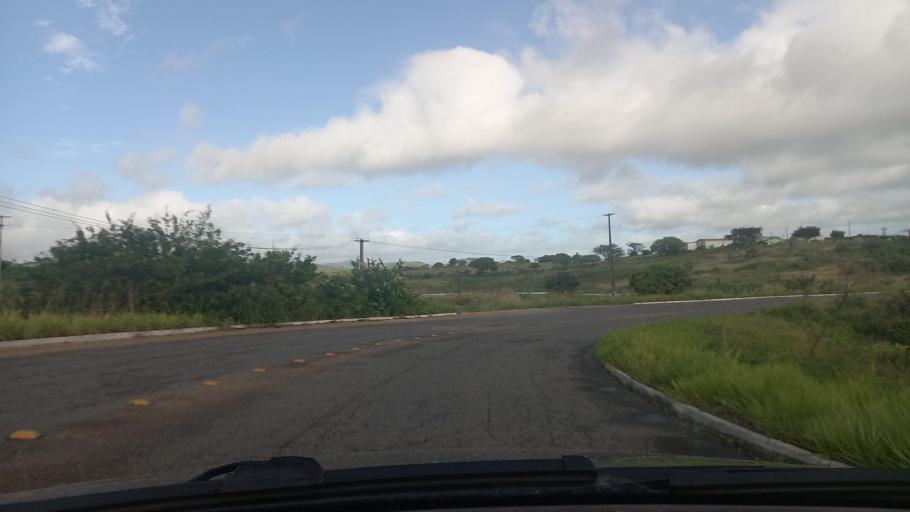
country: BR
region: Pernambuco
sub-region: Pombos
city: Pombos
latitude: -8.1298
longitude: -35.3519
